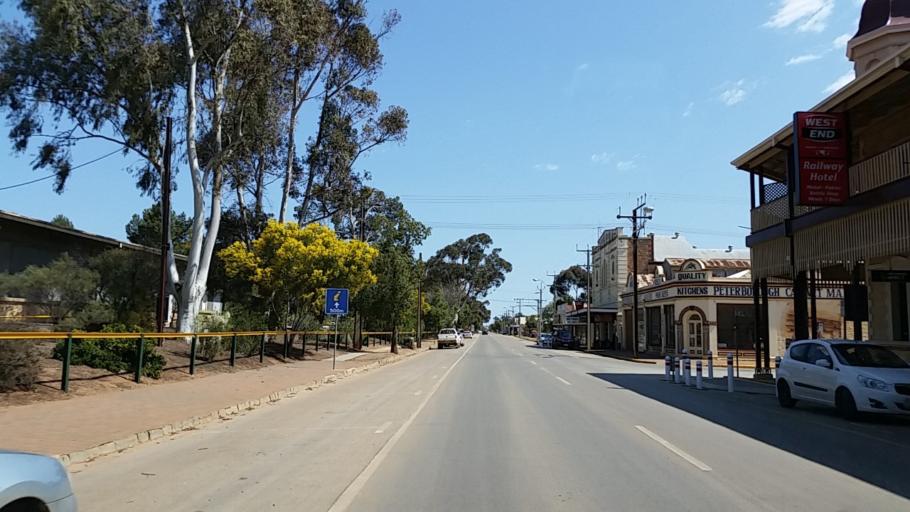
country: AU
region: South Australia
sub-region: Peterborough
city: Peterborough
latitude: -32.9736
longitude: 138.8353
